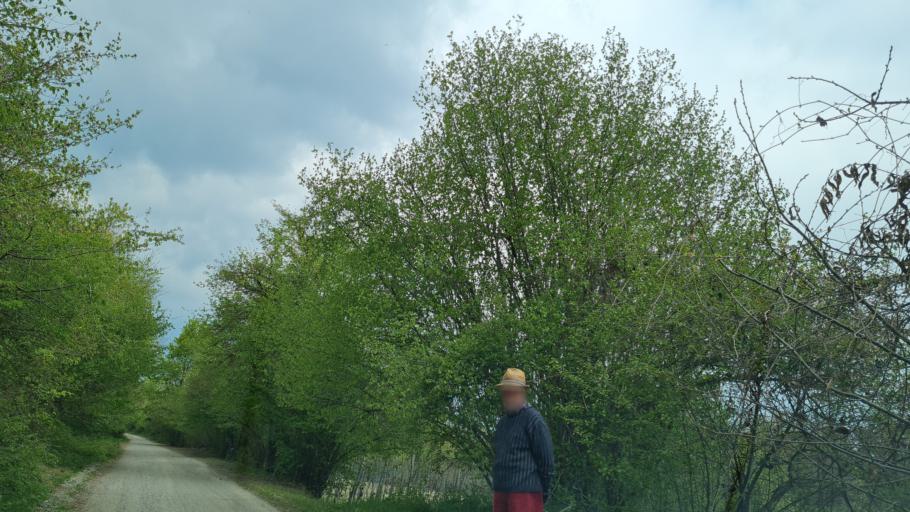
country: IT
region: Piedmont
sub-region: Provincia di Biella
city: Cerrione
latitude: 45.4735
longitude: 8.0628
